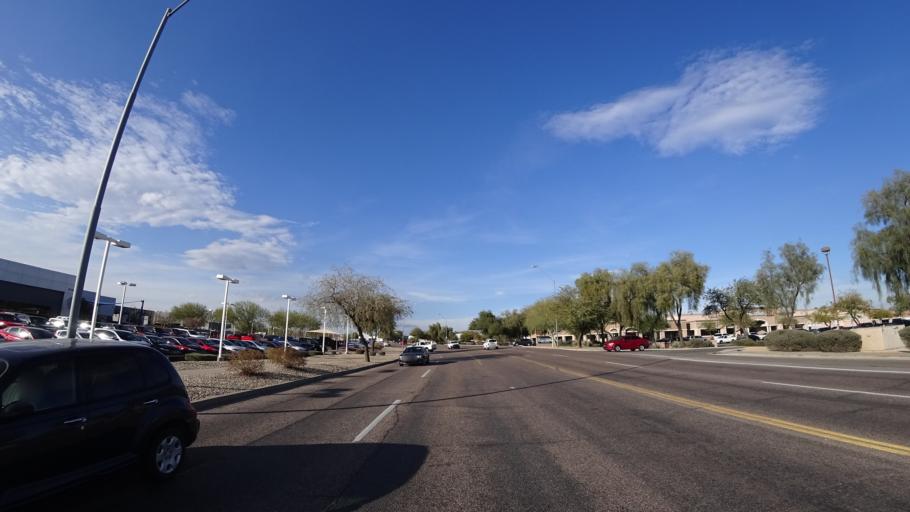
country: US
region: Arizona
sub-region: Maricopa County
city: Sun City
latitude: 33.6386
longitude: -112.2529
